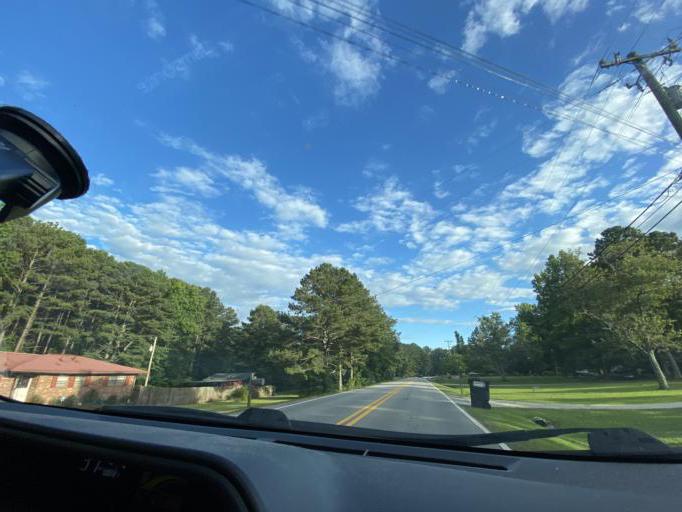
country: US
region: Georgia
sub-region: Fayette County
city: Peachtree City
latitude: 33.4319
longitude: -84.6482
